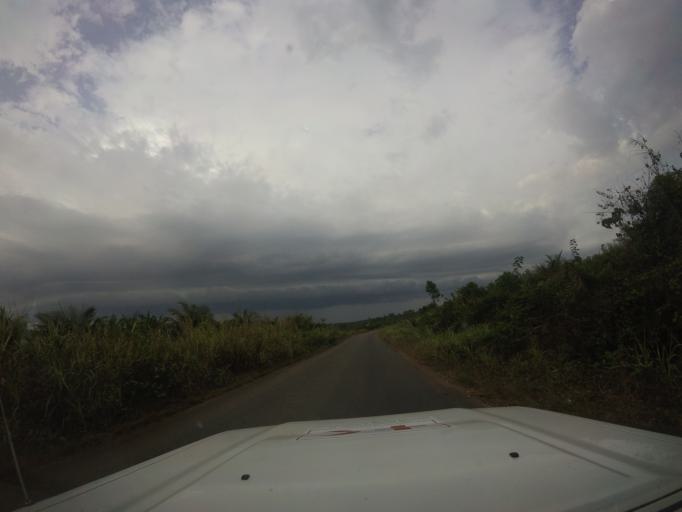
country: LR
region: Bomi
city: Tubmanburg
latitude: 6.7131
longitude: -10.9409
